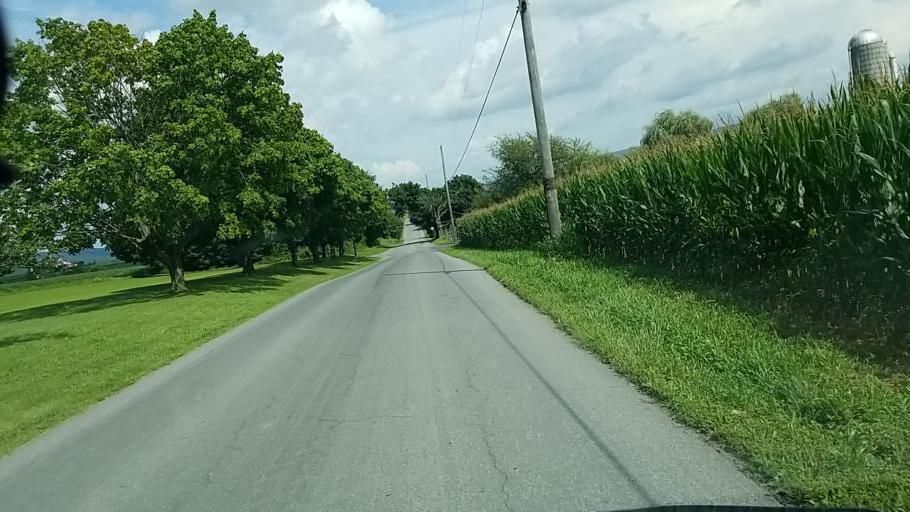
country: US
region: Pennsylvania
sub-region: Dauphin County
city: Elizabethville
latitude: 40.6122
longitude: -76.8322
